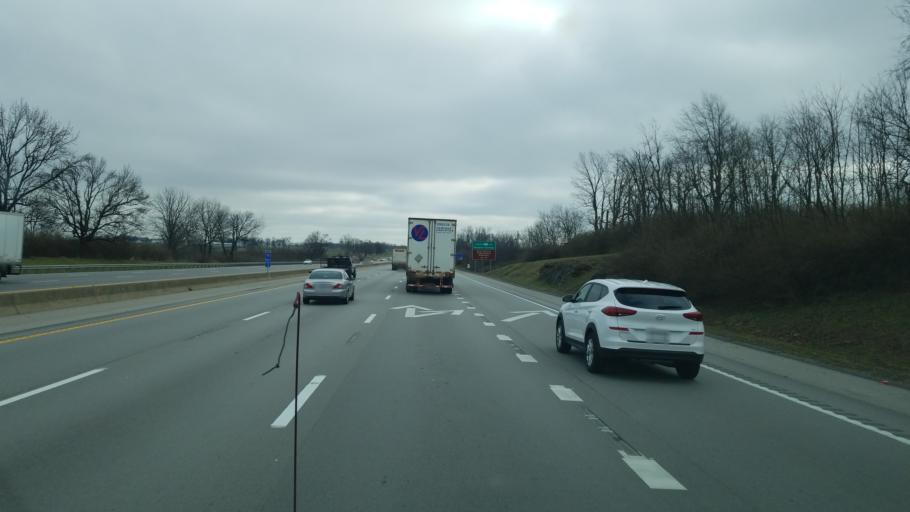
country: US
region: Kentucky
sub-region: Fayette County
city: Lexington-Fayette
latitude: 38.1087
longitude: -84.5043
